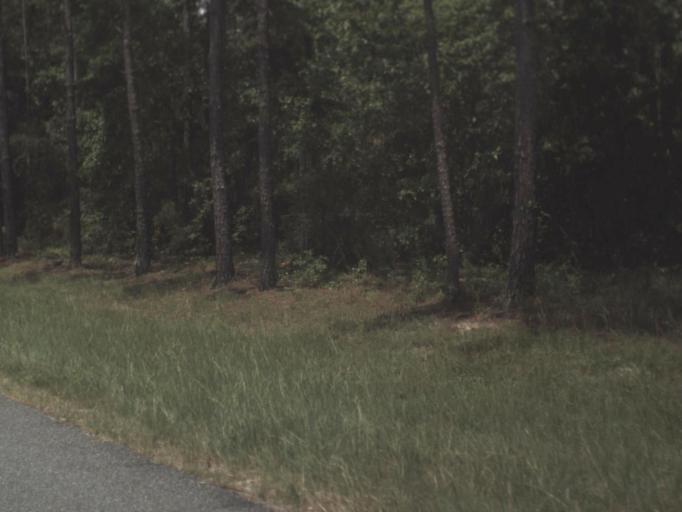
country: US
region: Florida
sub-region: Hamilton County
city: Jasper
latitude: 30.5031
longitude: -83.0706
